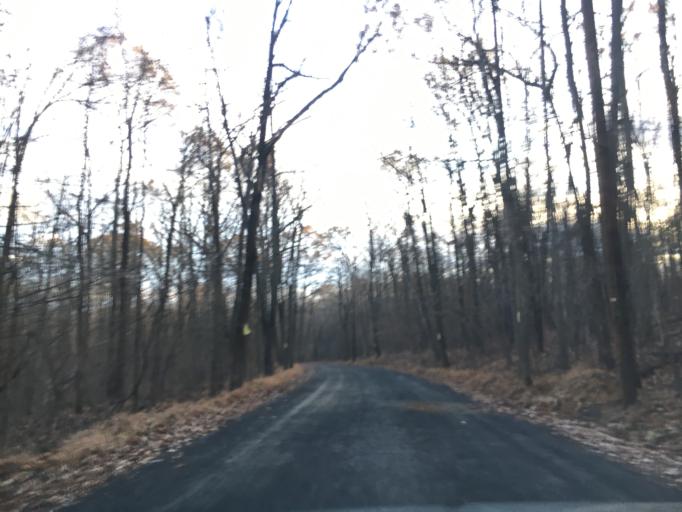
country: US
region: Pennsylvania
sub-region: Carbon County
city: Lehighton
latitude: 40.7614
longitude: -75.6937
